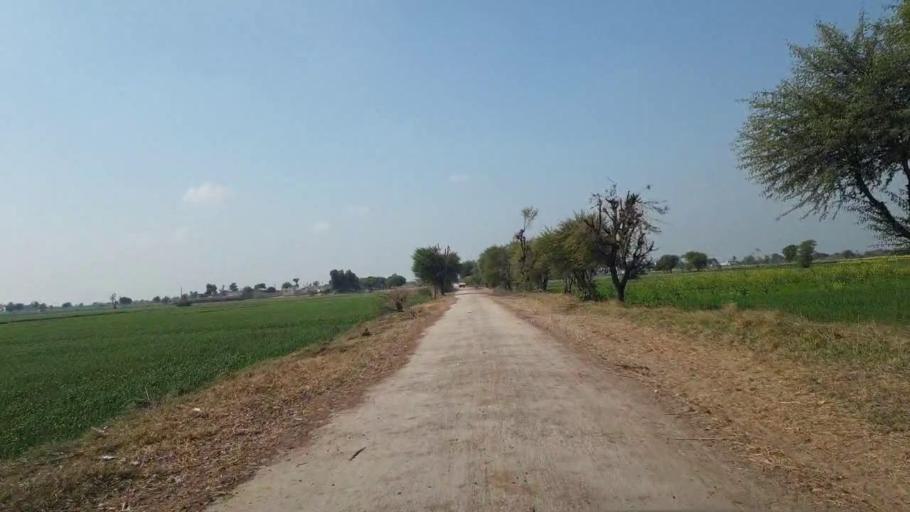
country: PK
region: Sindh
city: Shahdadpur
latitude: 26.0412
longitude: 68.5868
